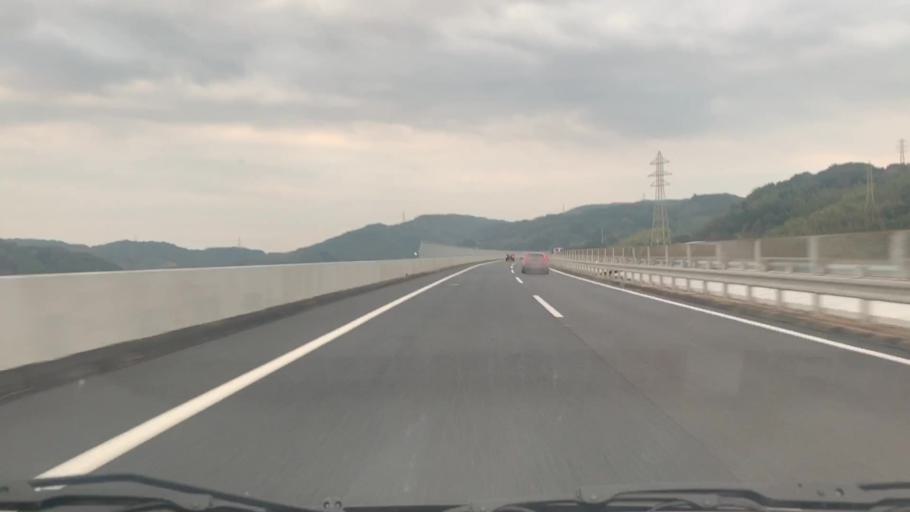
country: JP
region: Nagasaki
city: Omura
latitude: 32.8902
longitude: 129.9897
